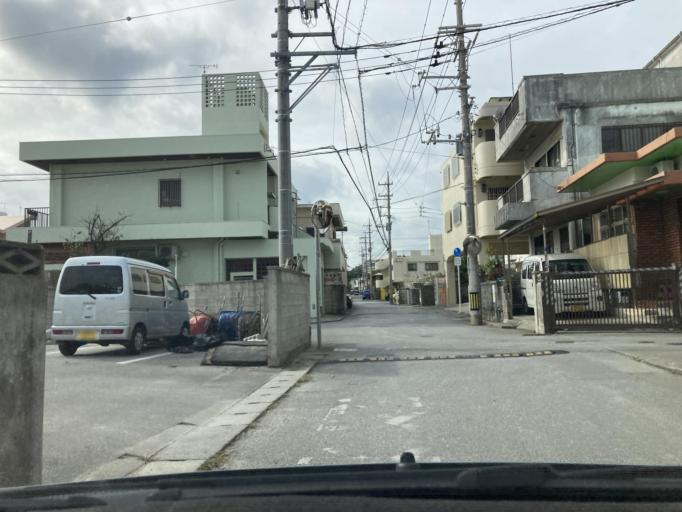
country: JP
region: Okinawa
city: Ginowan
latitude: 26.2069
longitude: 127.7545
